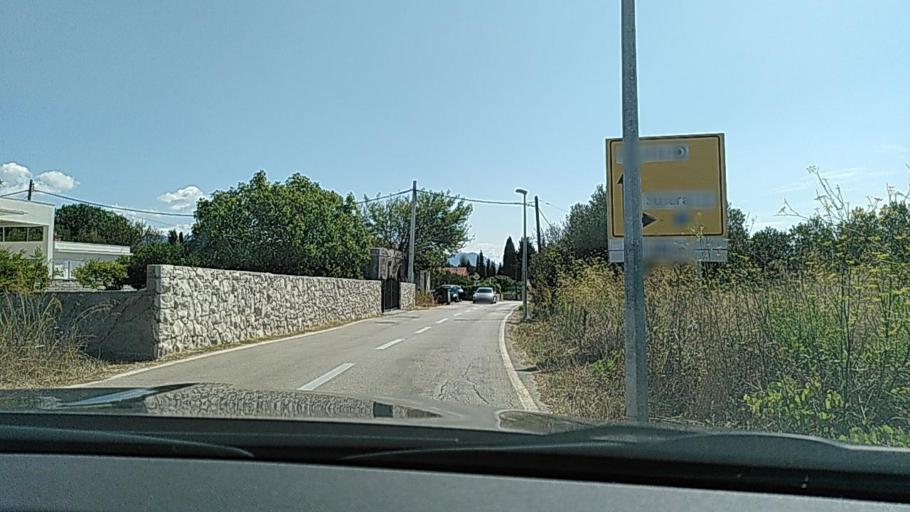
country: HR
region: Dubrovacko-Neretvanska
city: Orebic
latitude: 43.1280
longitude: 17.1821
